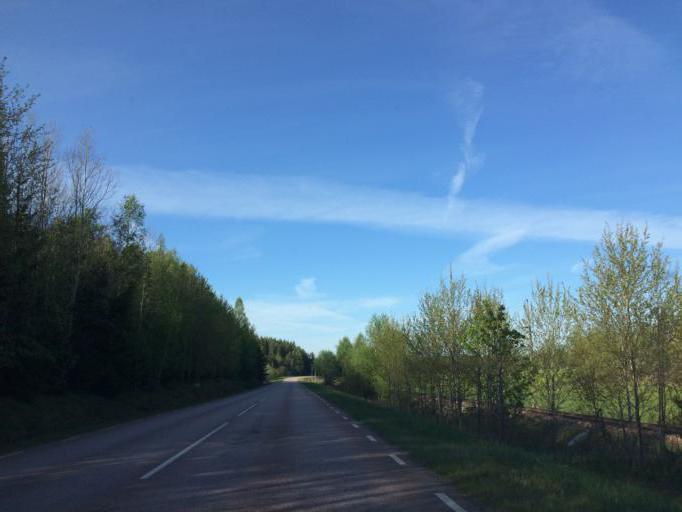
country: SE
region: Soedermanland
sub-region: Eskilstuna Kommun
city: Kvicksund
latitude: 59.4144
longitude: 16.2761
